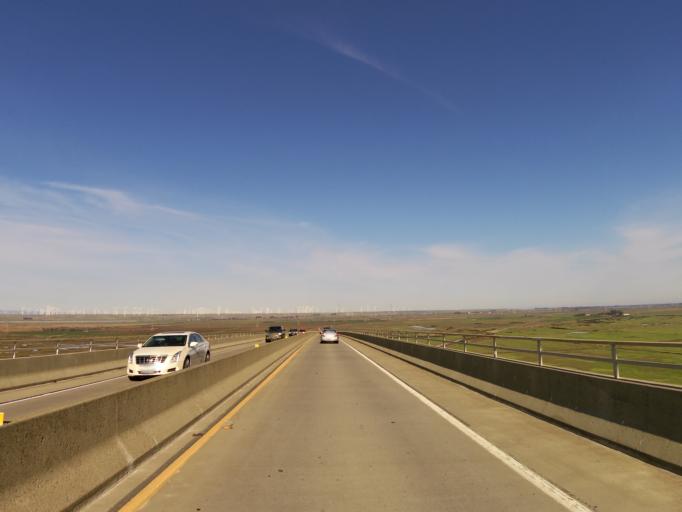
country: US
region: California
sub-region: Contra Costa County
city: Oakley
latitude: 38.0303
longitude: -121.7516
